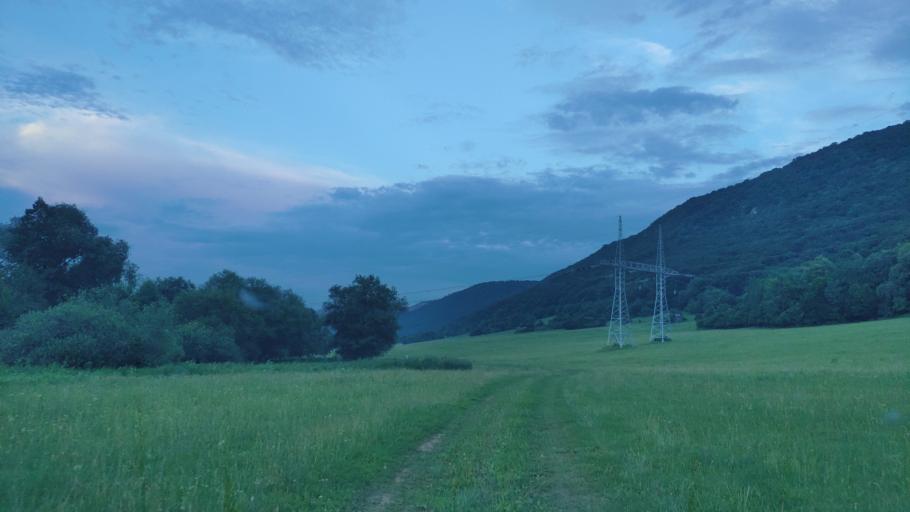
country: SK
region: Kosicky
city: Medzev
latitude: 48.5838
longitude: 20.7665
